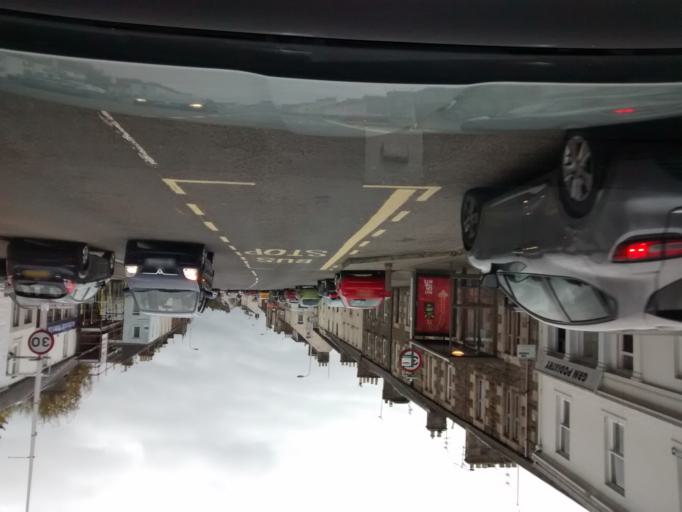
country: GB
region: Scotland
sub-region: Perth and Kinross
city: Auchterarder
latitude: 56.2948
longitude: -3.7110
